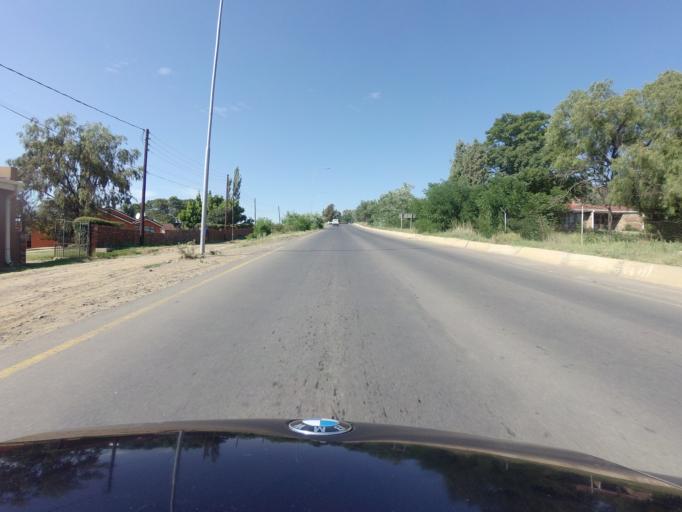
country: LS
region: Maseru
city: Maseru
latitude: -29.2951
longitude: 27.5064
